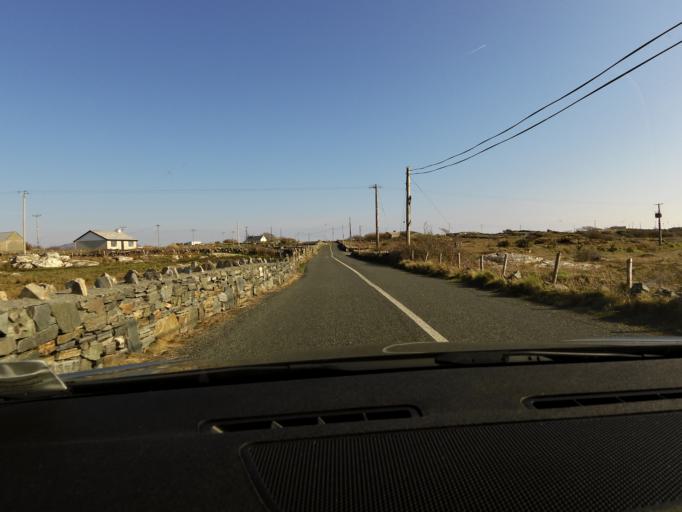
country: IE
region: Connaught
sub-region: County Galway
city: Clifden
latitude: 53.4271
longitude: -10.0713
